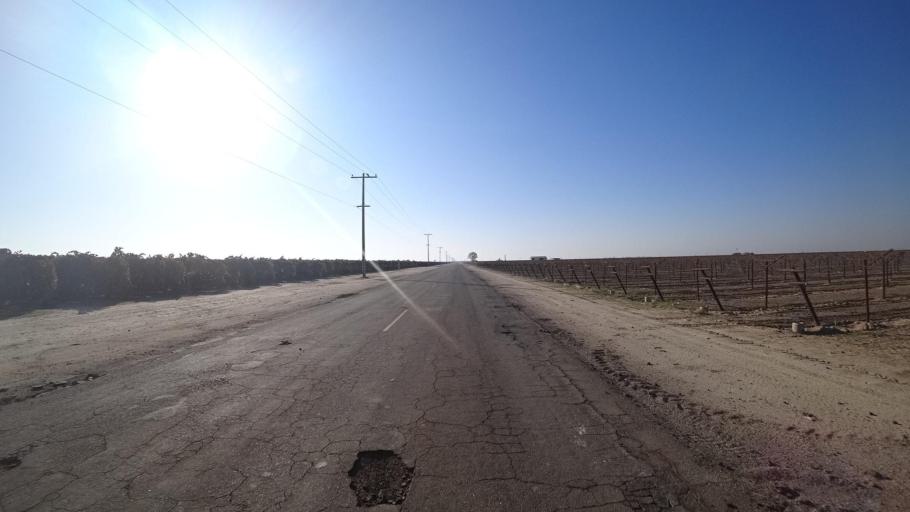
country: US
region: California
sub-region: Kern County
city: McFarland
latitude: 35.7265
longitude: -119.1695
